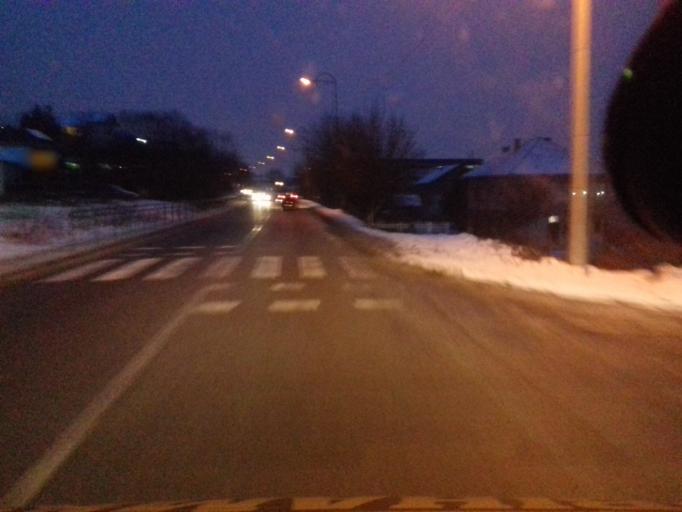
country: BA
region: Federation of Bosnia and Herzegovina
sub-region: Kanton Sarajevo
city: Sarajevo
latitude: 43.8602
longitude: 18.3192
